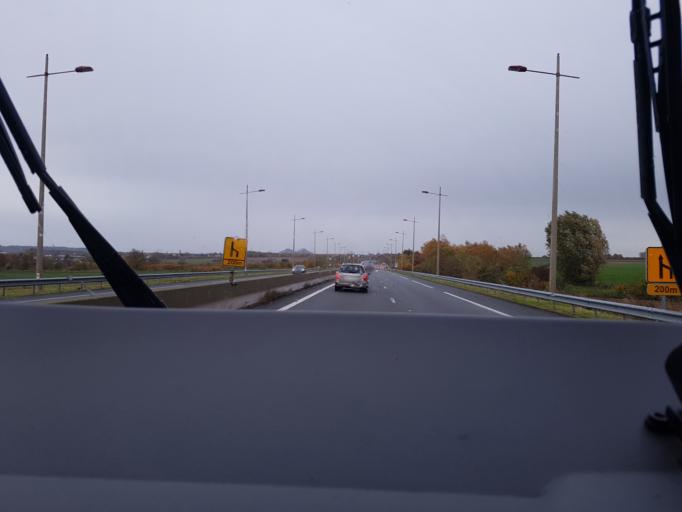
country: FR
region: Nord-Pas-de-Calais
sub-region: Departement du Pas-de-Calais
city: Sains-en-Gohelle
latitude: 50.4354
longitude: 2.6845
